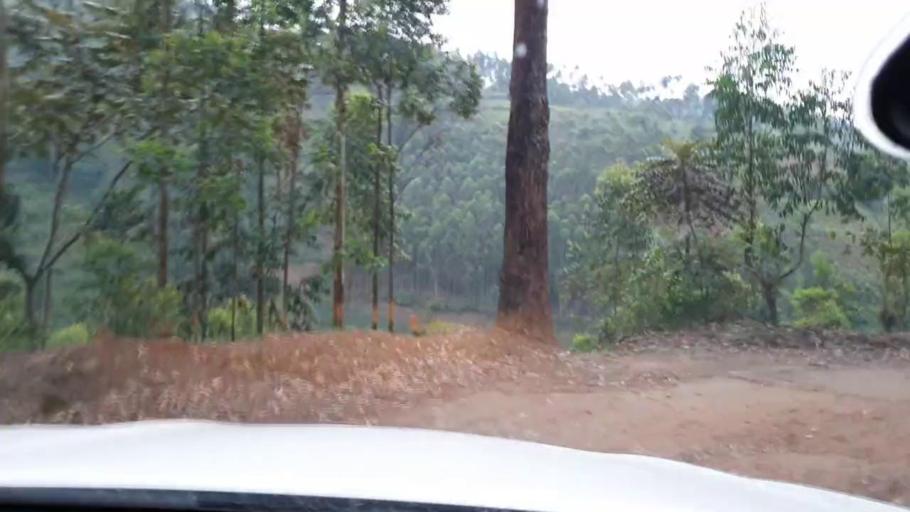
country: RW
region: Western Province
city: Cyangugu
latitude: -2.4129
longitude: 29.1954
